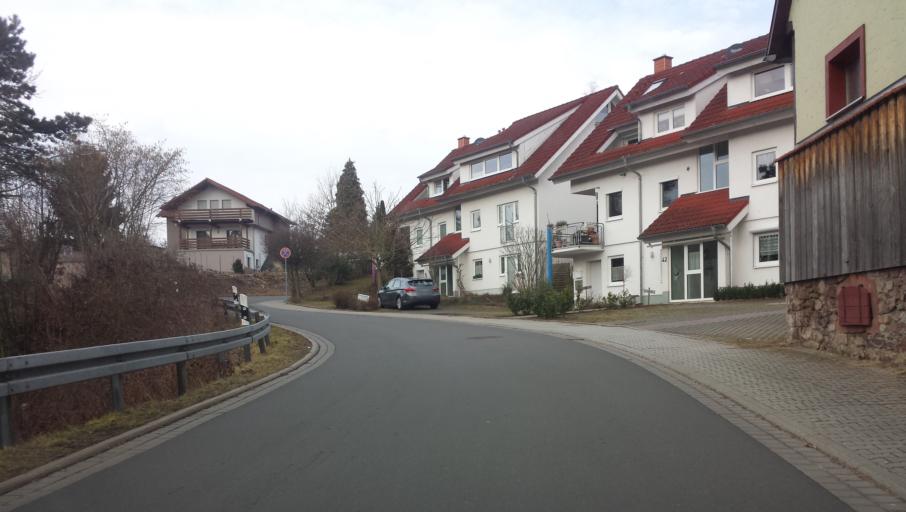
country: DE
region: Hesse
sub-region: Regierungsbezirk Darmstadt
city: Brensbach
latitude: 49.7906
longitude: 8.9301
